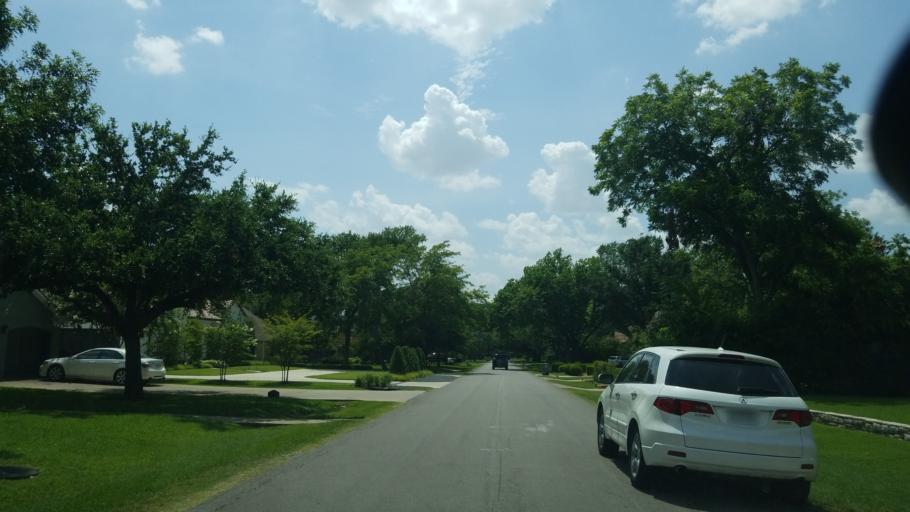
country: US
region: Texas
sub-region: Dallas County
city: University Park
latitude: 32.8695
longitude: -96.7977
